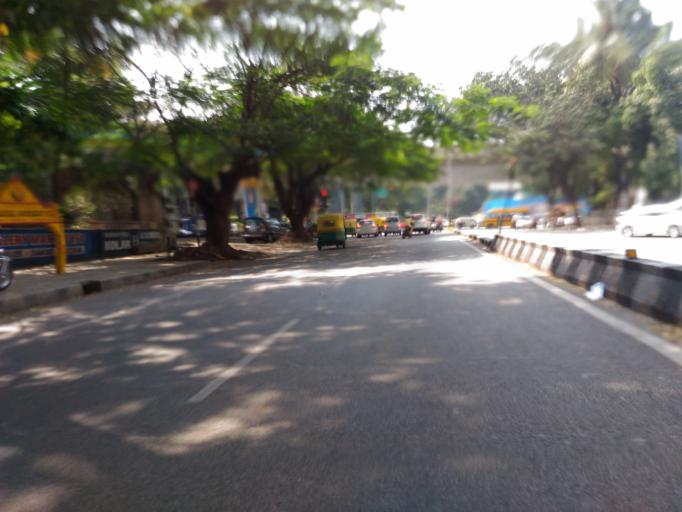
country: IN
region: Karnataka
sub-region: Bangalore Urban
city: Bangalore
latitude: 12.9367
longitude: 77.5809
